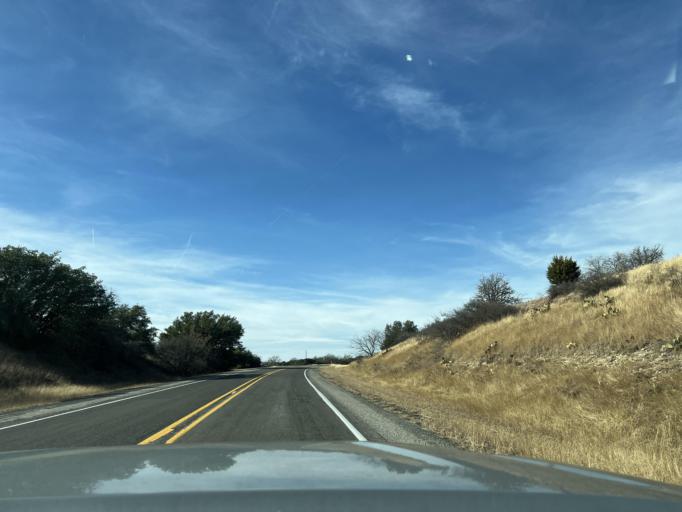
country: US
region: Texas
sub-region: Eastland County
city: Cisco
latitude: 32.4648
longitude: -99.0317
